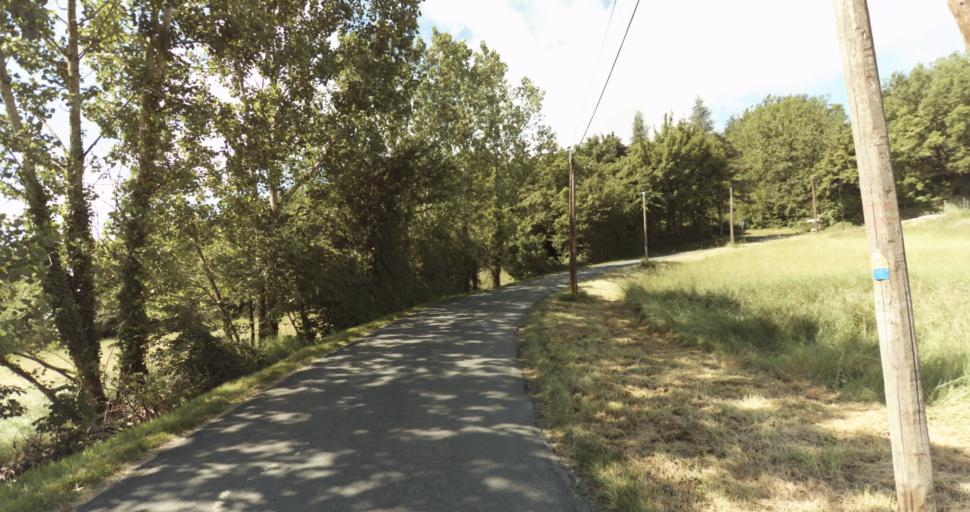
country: FR
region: Aquitaine
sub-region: Departement de la Dordogne
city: Le Bugue
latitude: 44.8434
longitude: 0.9013
